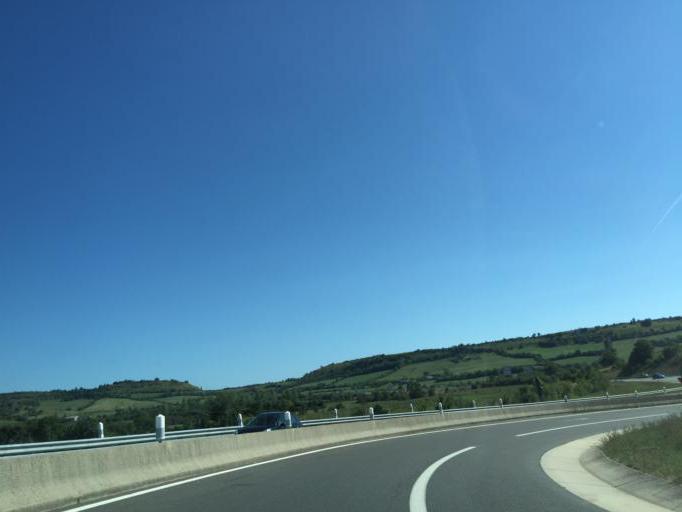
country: FR
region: Midi-Pyrenees
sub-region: Departement de l'Aveyron
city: Severac-le-Chateau
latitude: 44.3320
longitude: 3.0866
